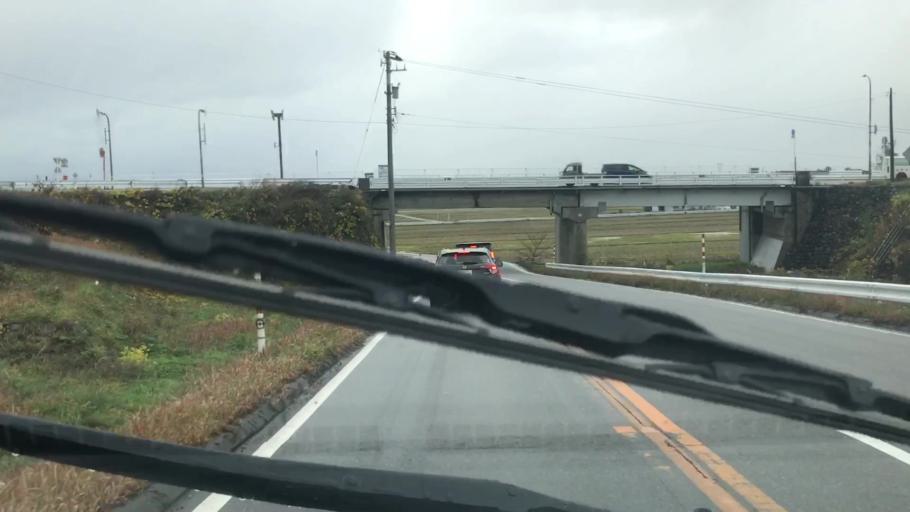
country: JP
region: Toyama
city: Toyama-shi
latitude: 36.6719
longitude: 137.2864
